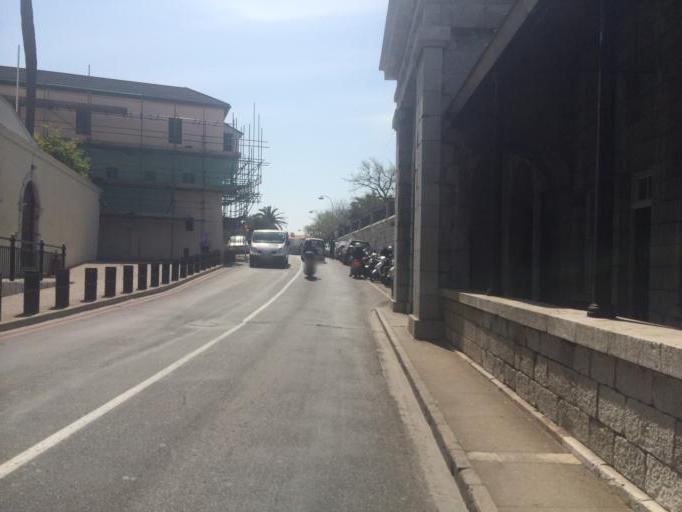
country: GI
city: Gibraltar
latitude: 36.1394
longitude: -5.3547
